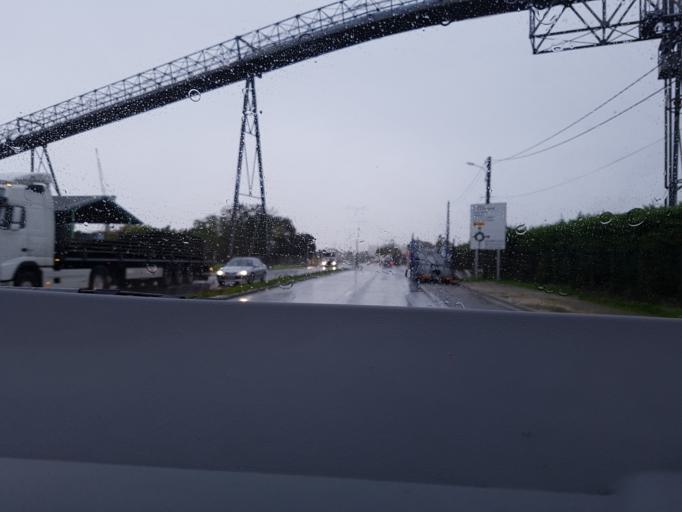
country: FR
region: Aquitaine
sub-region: Departement de la Gironde
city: Bassens
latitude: 44.8977
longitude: -0.5314
